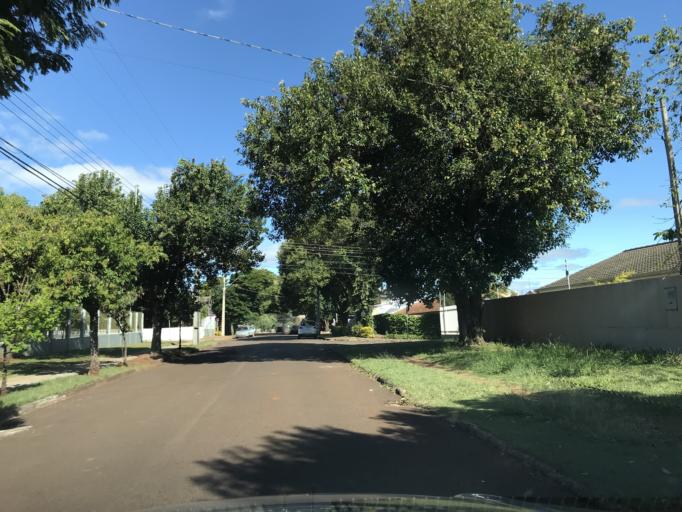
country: BR
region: Parana
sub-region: Cascavel
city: Cascavel
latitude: -24.9401
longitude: -53.4683
